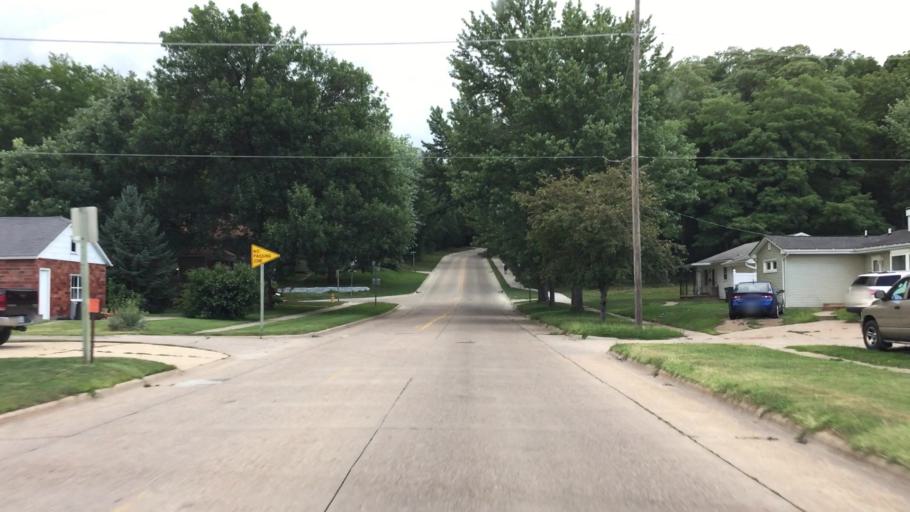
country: US
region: Iowa
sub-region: Lee County
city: Fort Madison
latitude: 40.6356
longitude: -91.3245
